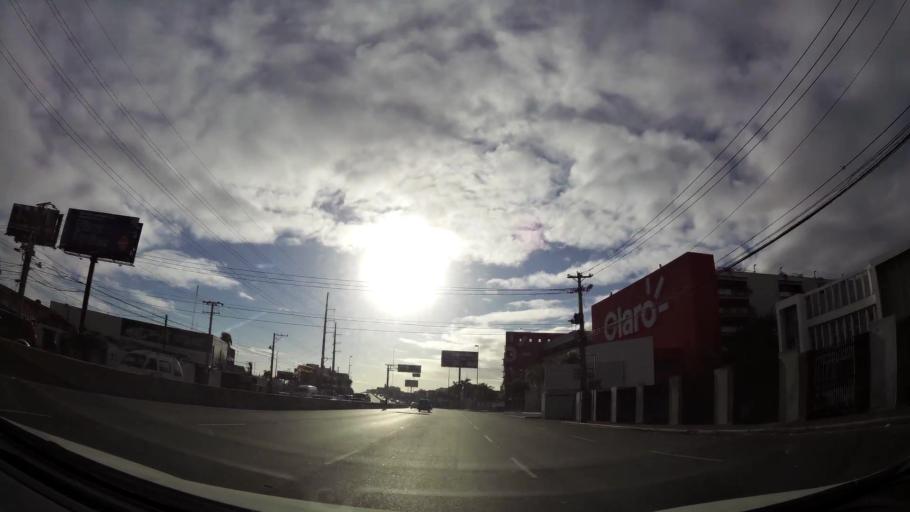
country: DO
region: Nacional
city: La Julia
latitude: 18.4833
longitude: -69.9352
